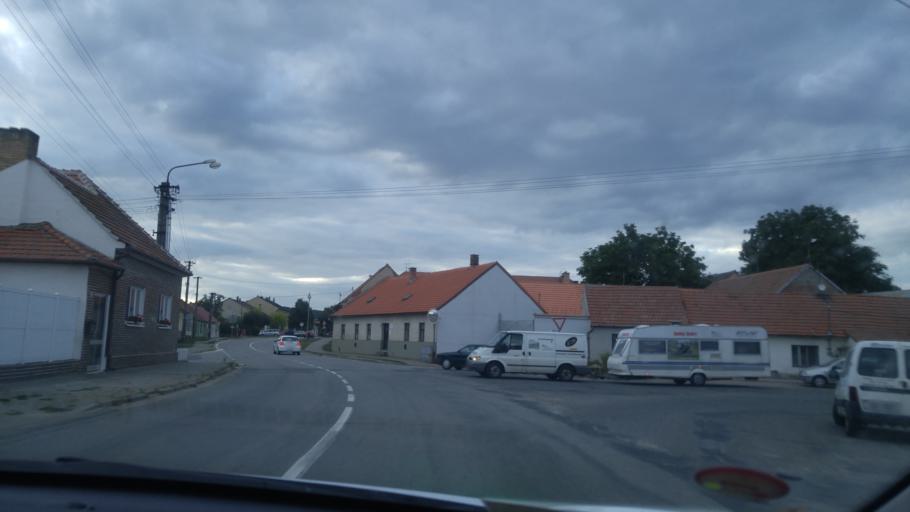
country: CZ
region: South Moravian
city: Ricany
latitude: 49.2098
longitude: 16.4118
